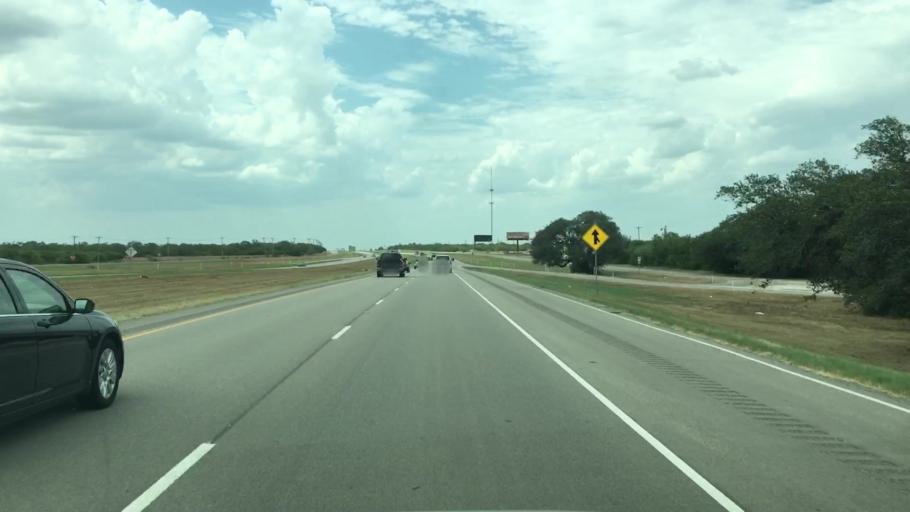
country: US
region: Texas
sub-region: Live Oak County
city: Three Rivers
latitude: 28.4906
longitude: -98.1444
